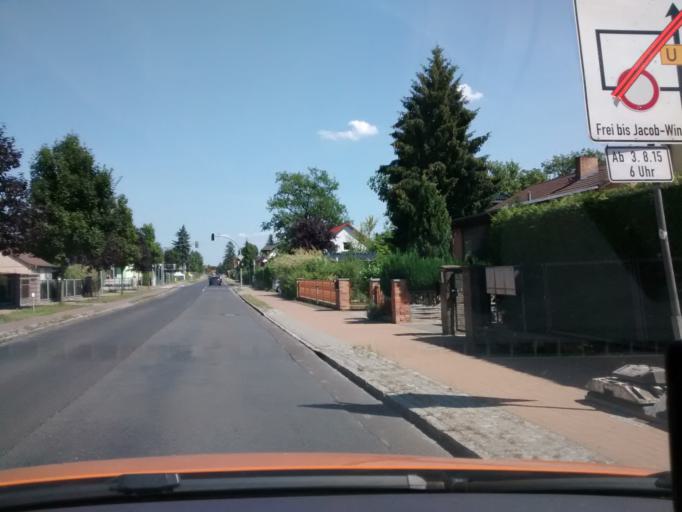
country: DE
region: Brandenburg
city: Hohen Neuendorf
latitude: 52.6666
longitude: 13.2722
